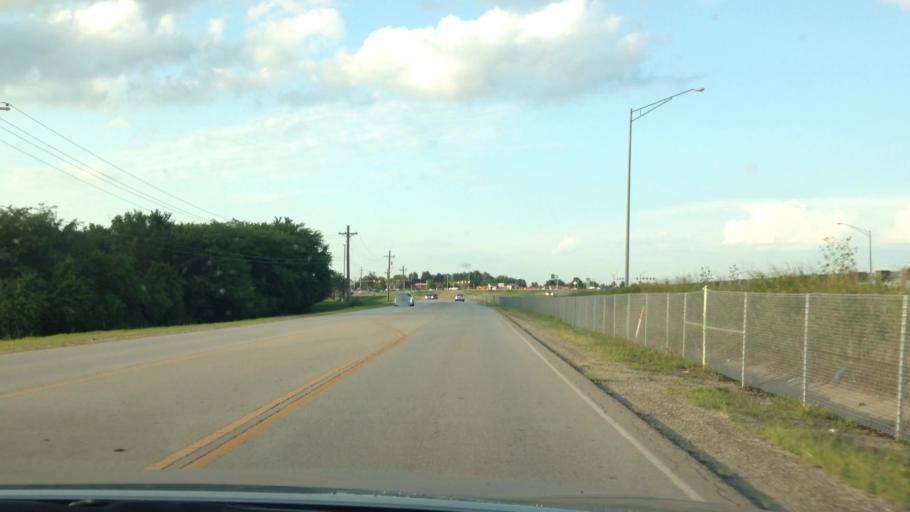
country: US
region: Missouri
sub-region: Clay County
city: Liberty
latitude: 39.2613
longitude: -94.4494
